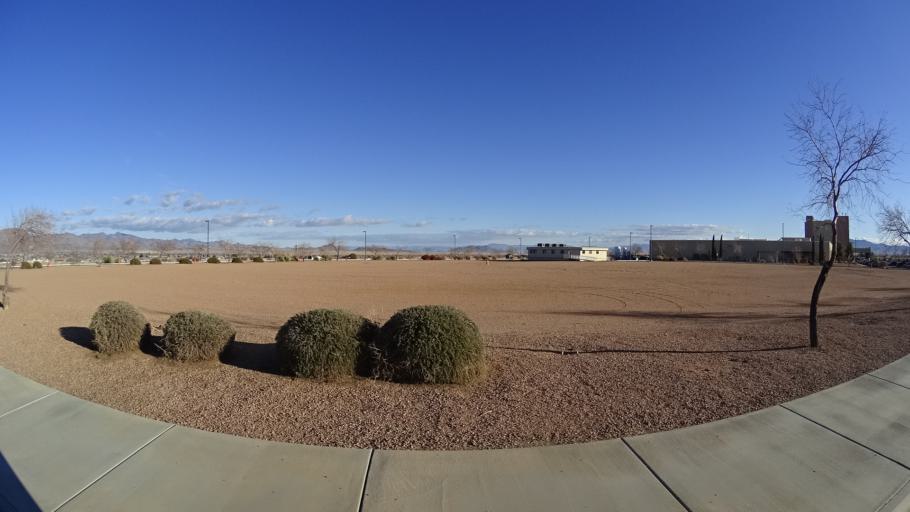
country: US
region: Arizona
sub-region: Mohave County
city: New Kingman-Butler
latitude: 35.2179
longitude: -113.9878
